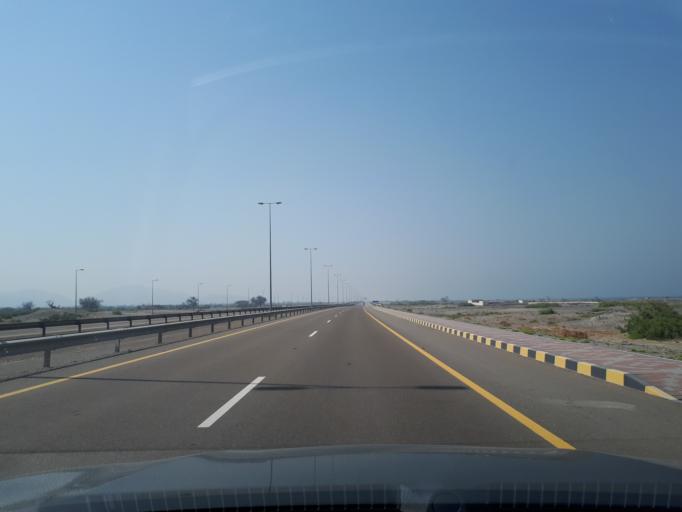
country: AE
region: Al Fujayrah
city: Al Fujayrah
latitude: 24.9280
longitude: 56.3847
